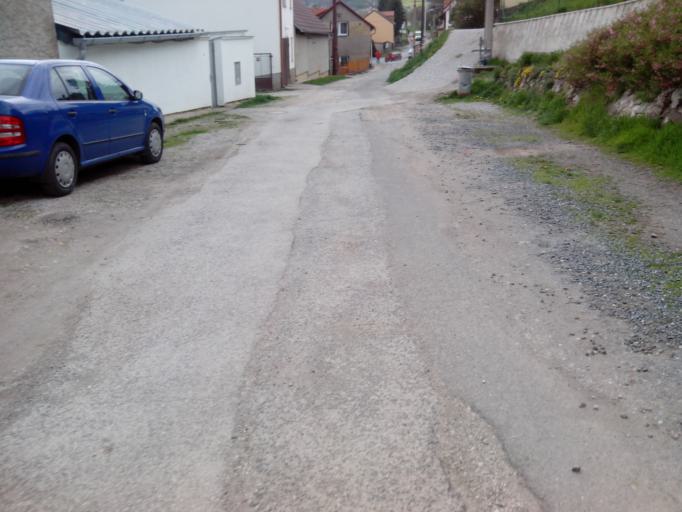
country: CZ
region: Central Bohemia
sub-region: Okres Beroun
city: Kraluv Dvur
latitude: 49.9539
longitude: 14.0263
